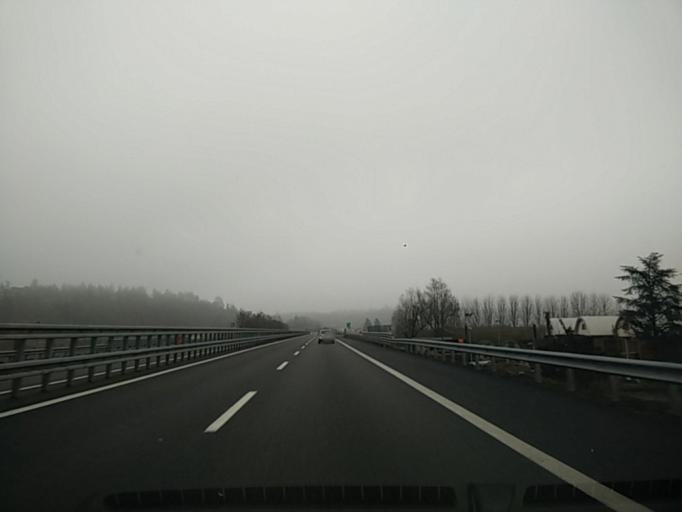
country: IT
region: Piedmont
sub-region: Provincia di Asti
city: Azzano d'Asti
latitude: 44.9085
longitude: 8.2725
